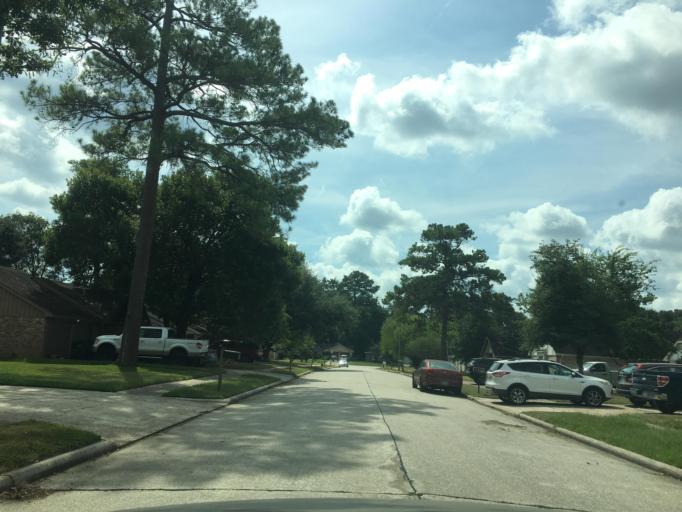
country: US
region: Texas
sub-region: Harris County
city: Spring
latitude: 30.1156
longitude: -95.3964
